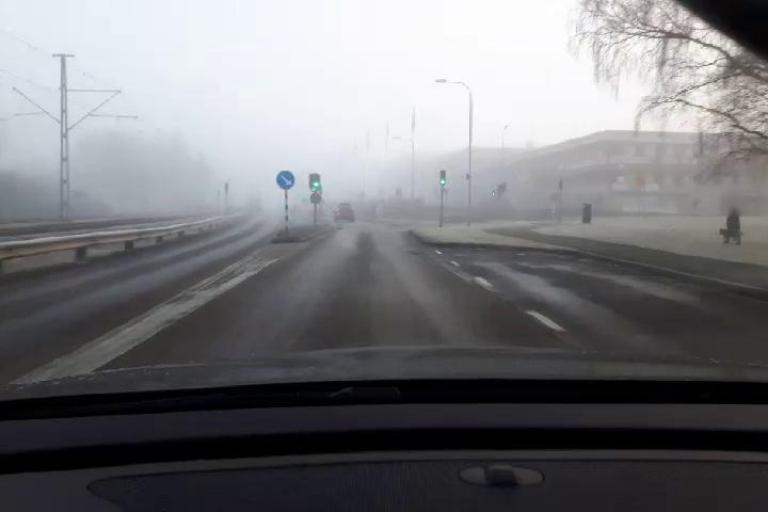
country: SE
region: Vaestra Goetaland
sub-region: Goteborg
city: Majorna
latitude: 57.6730
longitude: 11.8804
